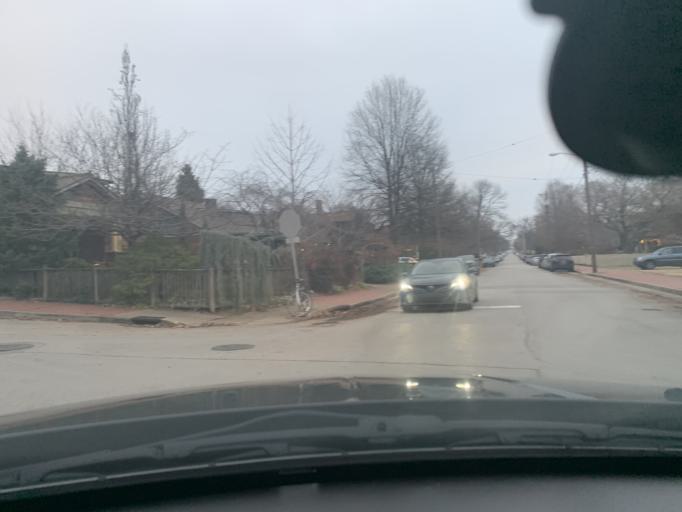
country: US
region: Tennessee
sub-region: Davidson County
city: Nashville
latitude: 36.1705
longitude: -86.7617
